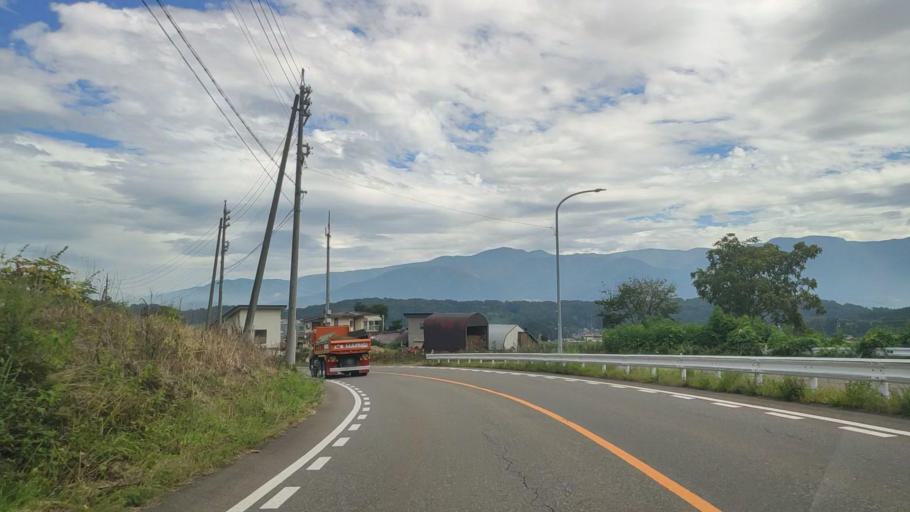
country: JP
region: Nagano
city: Iiyama
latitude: 36.8684
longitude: 138.3439
